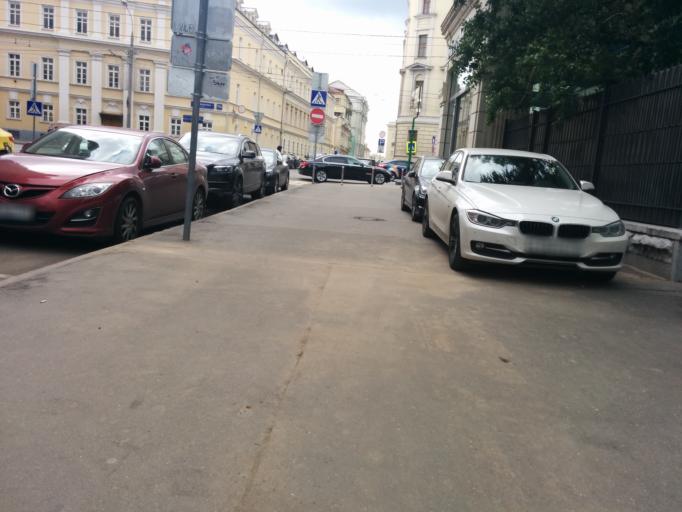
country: RU
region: Moscow
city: Moscow
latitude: 55.7531
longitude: 37.6058
